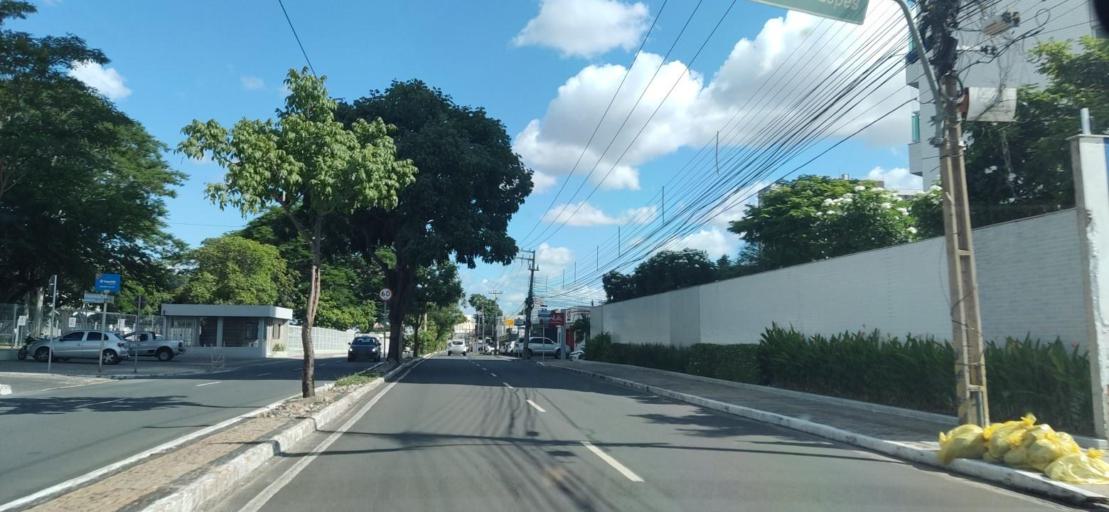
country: BR
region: Piaui
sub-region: Teresina
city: Teresina
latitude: -5.0767
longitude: -42.7909
